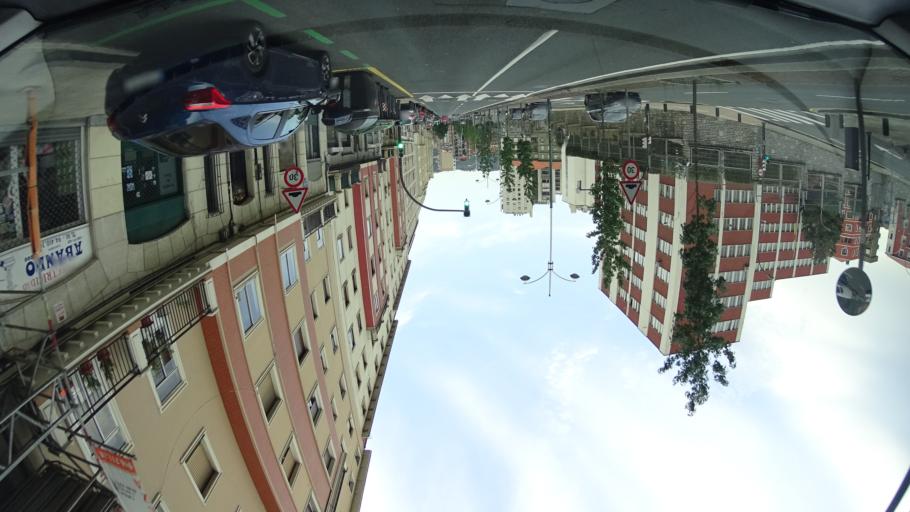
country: ES
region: Basque Country
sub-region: Bizkaia
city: Bilbao
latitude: 43.2536
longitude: -2.9340
